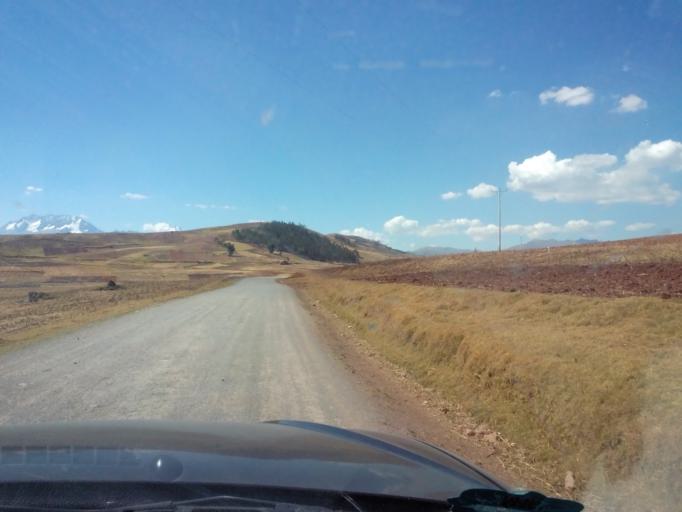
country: PE
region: Cusco
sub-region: Provincia de Anta
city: Huarocondo
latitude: -13.4057
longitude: -72.1606
